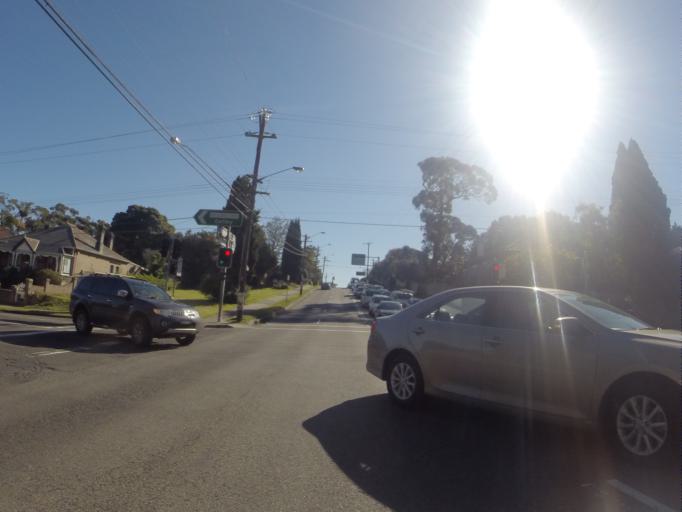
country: AU
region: New South Wales
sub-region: Kogarah
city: Hurstville Grove
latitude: -33.9707
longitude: 151.0988
